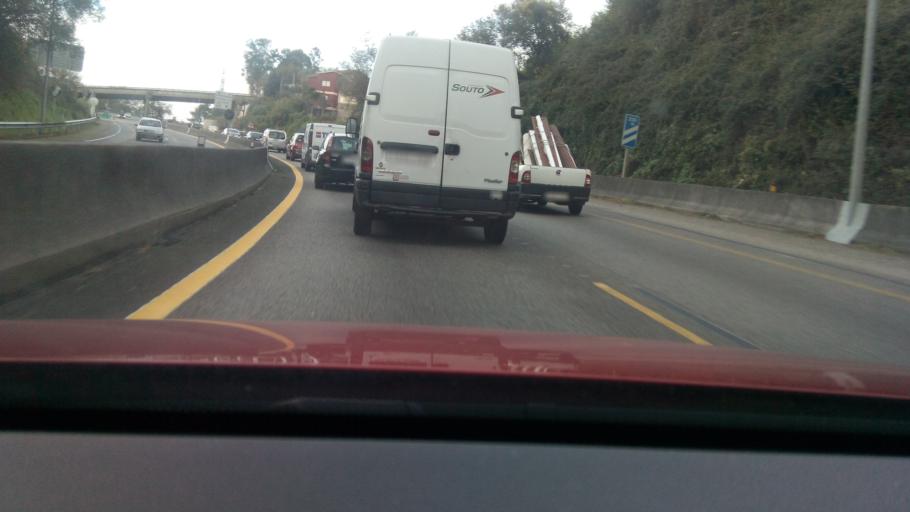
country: ES
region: Galicia
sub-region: Provincia de Pontevedra
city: Vigo
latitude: 42.2094
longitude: -8.6886
